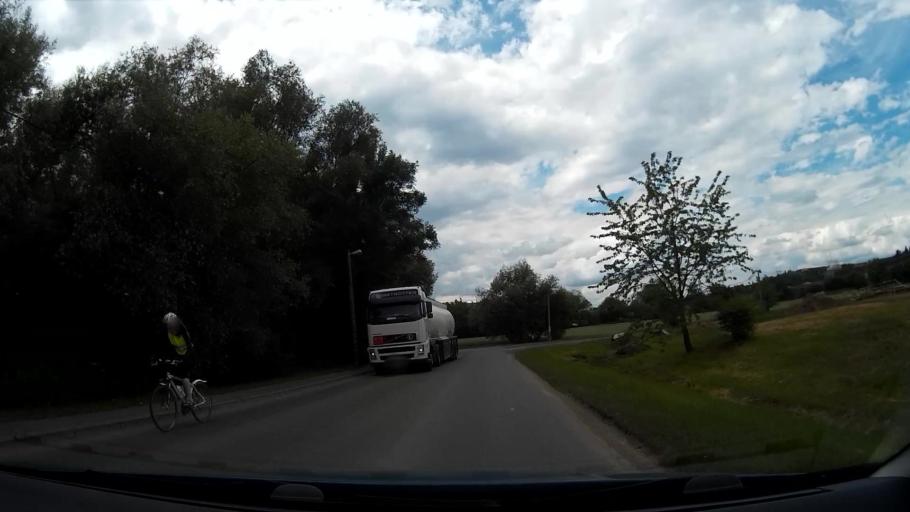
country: CZ
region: South Moravian
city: Troubsko
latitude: 49.1742
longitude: 16.5041
